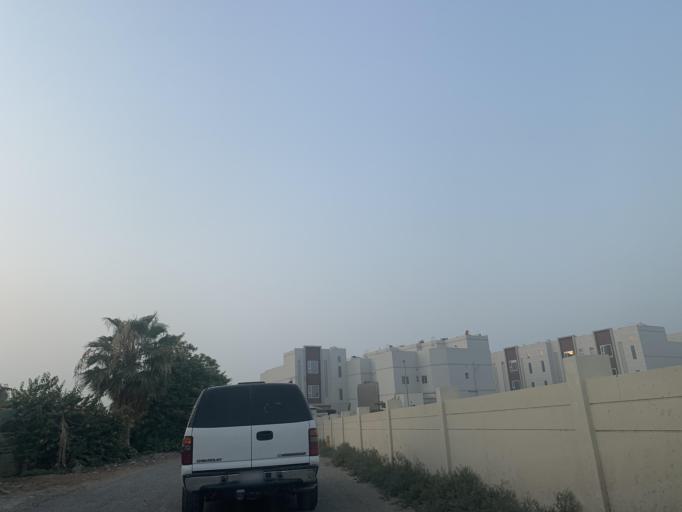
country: BH
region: Manama
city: Jidd Hafs
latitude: 26.2286
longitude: 50.5125
